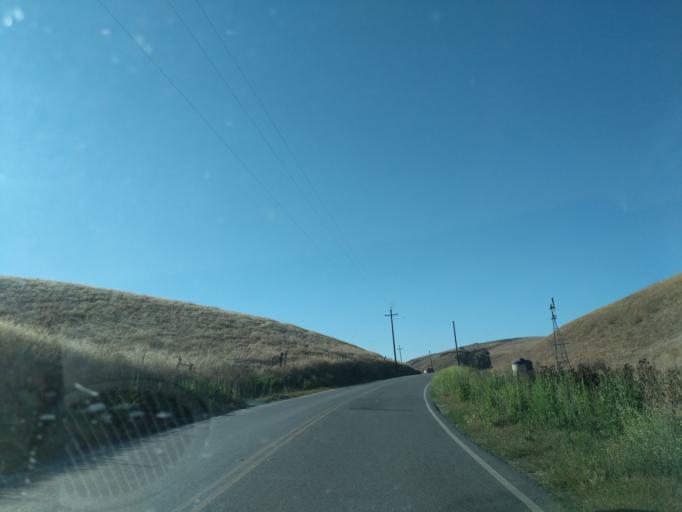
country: US
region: California
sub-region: San Benito County
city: Ridgemark
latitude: 36.8261
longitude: -121.3314
